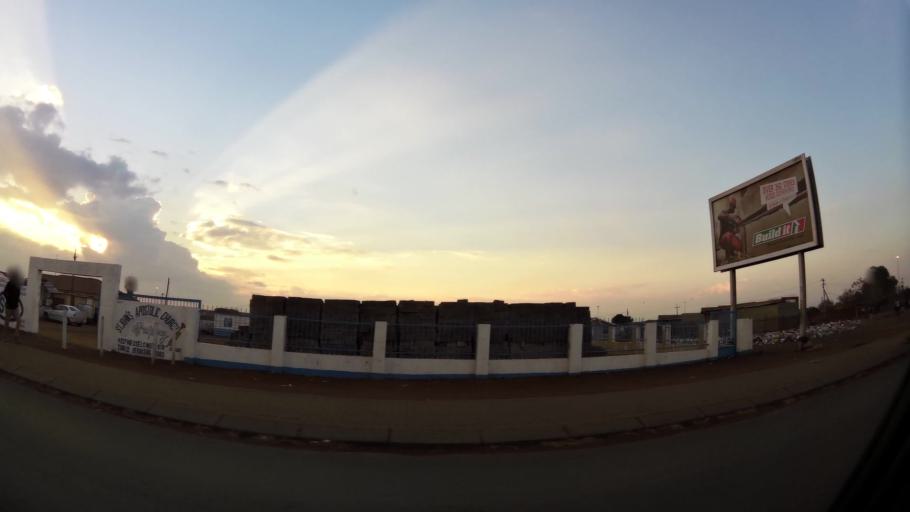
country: ZA
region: Gauteng
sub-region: City of Johannesburg Metropolitan Municipality
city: Orange Farm
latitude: -26.5705
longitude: 27.8433
